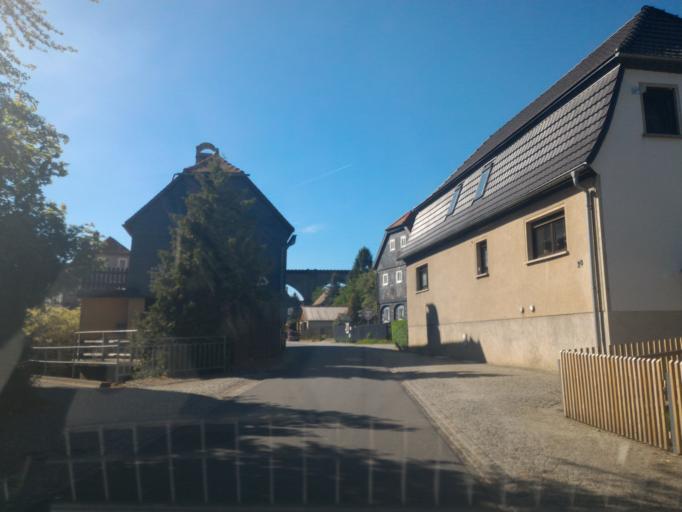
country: DE
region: Saxony
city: Niedercunnersdorf
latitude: 51.0382
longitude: 14.6665
